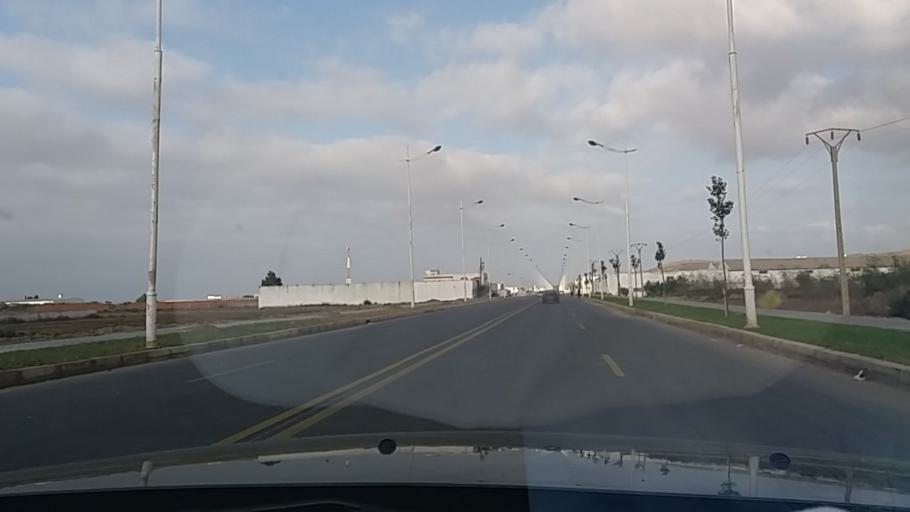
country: MA
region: Tanger-Tetouan
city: Tetouan
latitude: 35.5710
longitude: -5.3264
